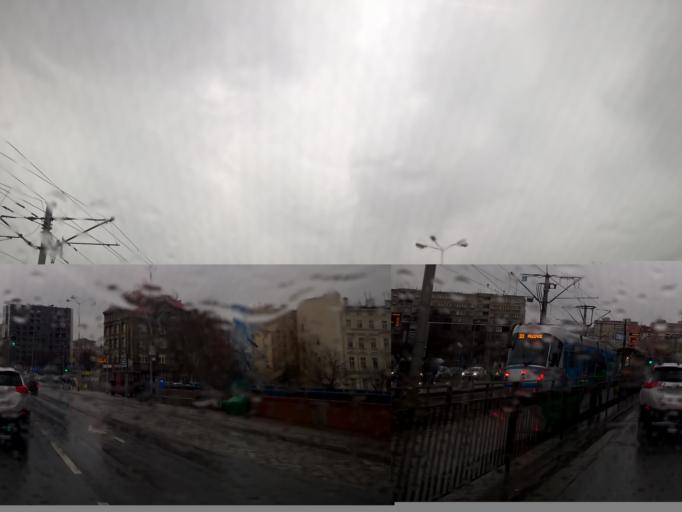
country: PL
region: Lower Silesian Voivodeship
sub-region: Powiat wroclawski
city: Wroclaw
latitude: 51.1121
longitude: 17.0206
